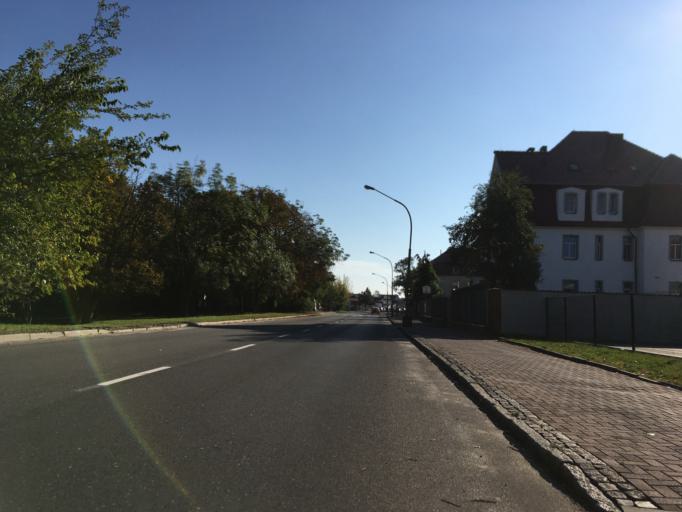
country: PL
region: Lubusz
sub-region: Powiat gorzowski
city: Kostrzyn nad Odra
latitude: 52.5924
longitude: 14.6535
